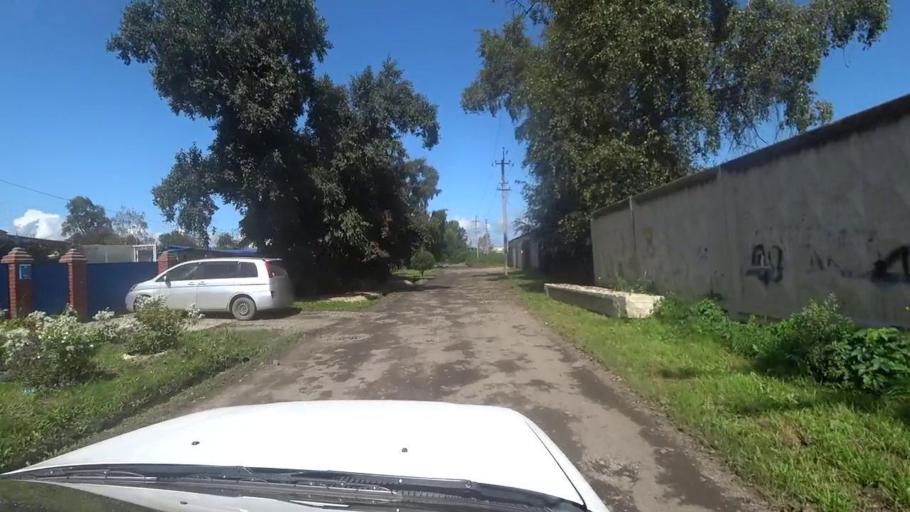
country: RU
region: Primorskiy
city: Dal'nerechensk
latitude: 45.9380
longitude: 133.7340
